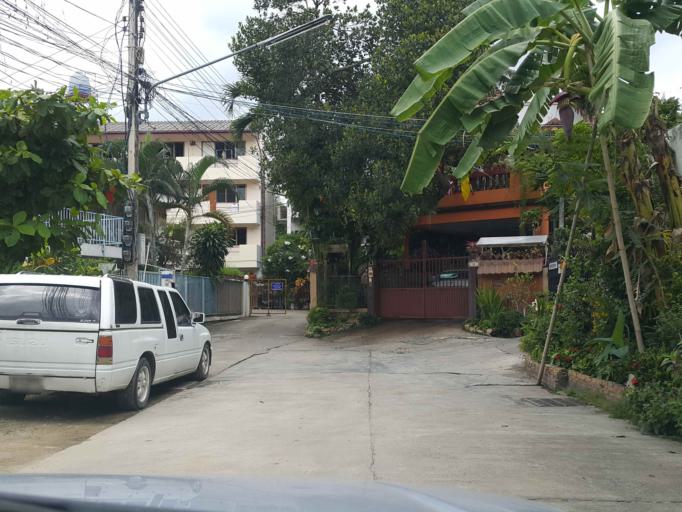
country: TH
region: Chiang Mai
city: Chiang Mai
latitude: 18.8010
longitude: 98.9651
